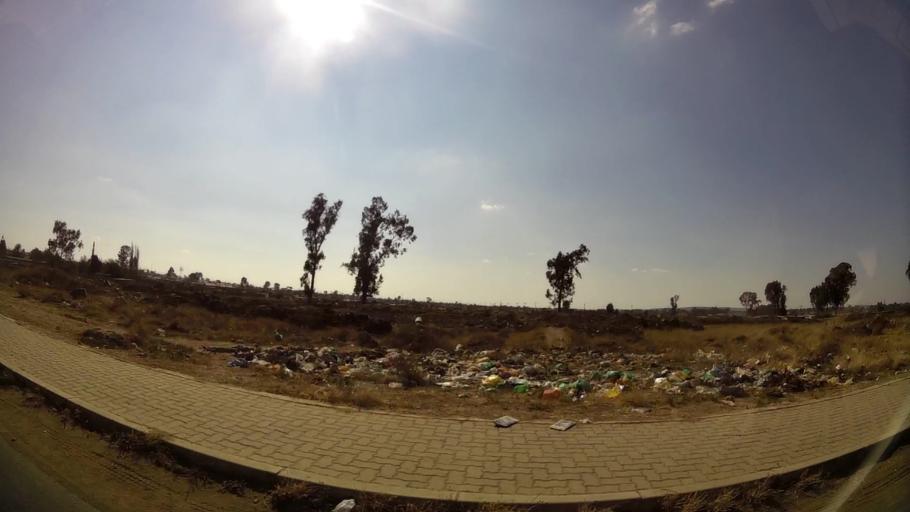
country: ZA
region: Orange Free State
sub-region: Mangaung Metropolitan Municipality
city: Bloemfontein
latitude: -29.1704
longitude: 26.2933
